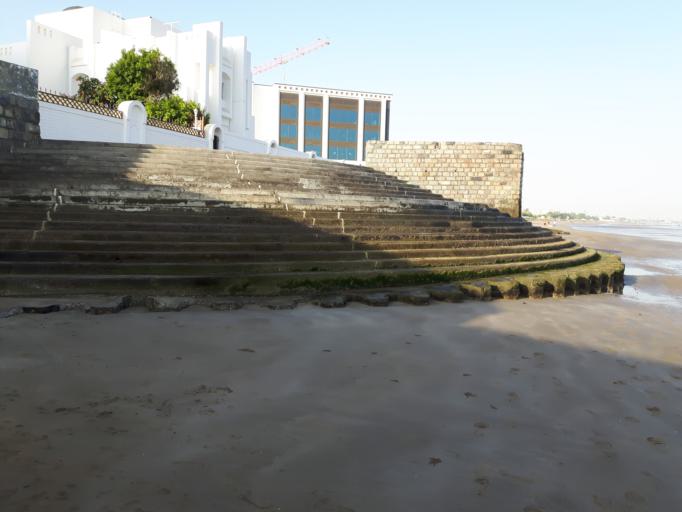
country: OM
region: Muhafazat Masqat
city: Bawshar
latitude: 23.6138
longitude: 58.4541
